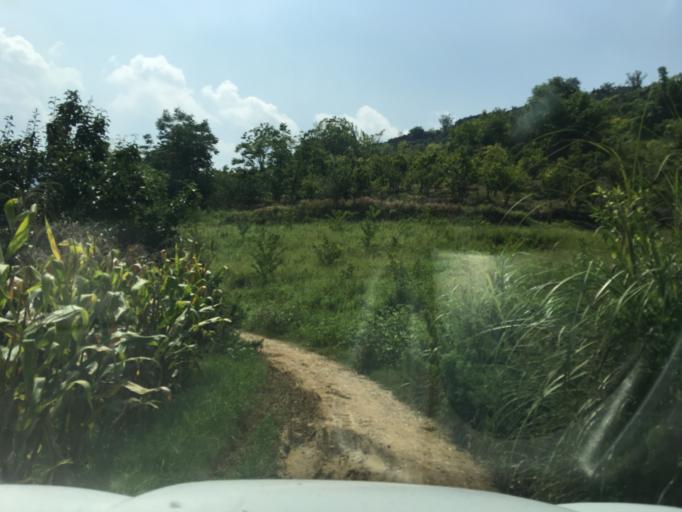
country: CN
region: Guangxi Zhuangzu Zizhiqu
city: Xinzhou
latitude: 24.9962
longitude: 105.7509
